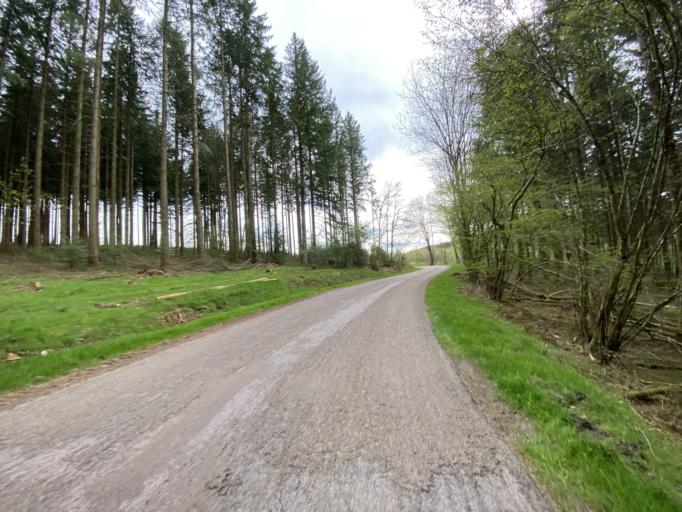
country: FR
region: Bourgogne
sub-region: Departement de la Cote-d'Or
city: Saulieu
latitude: 47.3102
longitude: 4.0895
